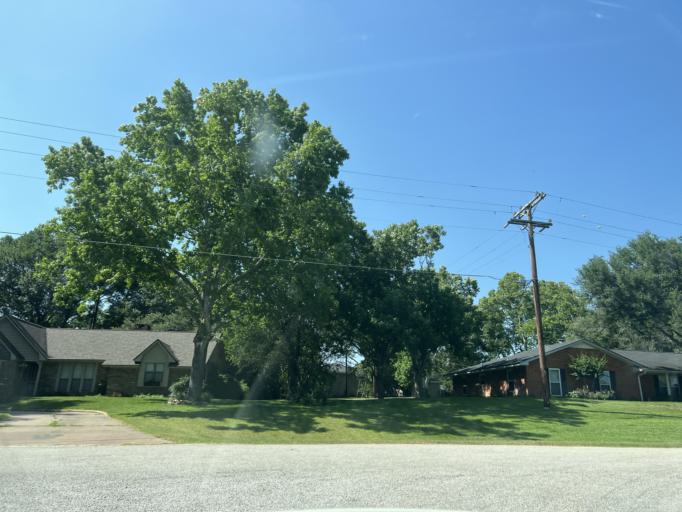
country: US
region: Texas
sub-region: Washington County
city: Brenham
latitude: 30.1518
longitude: -96.3651
